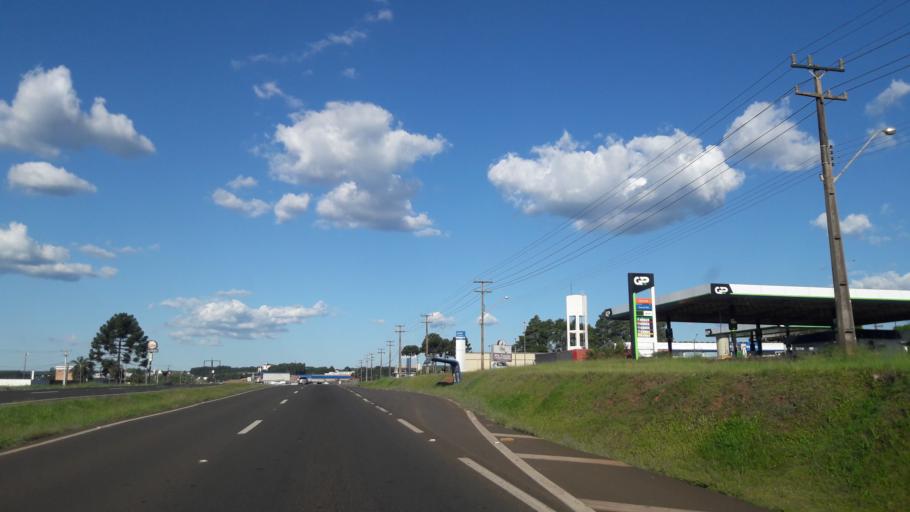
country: BR
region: Parana
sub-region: Guarapuava
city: Guarapuava
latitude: -25.3614
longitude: -51.4698
